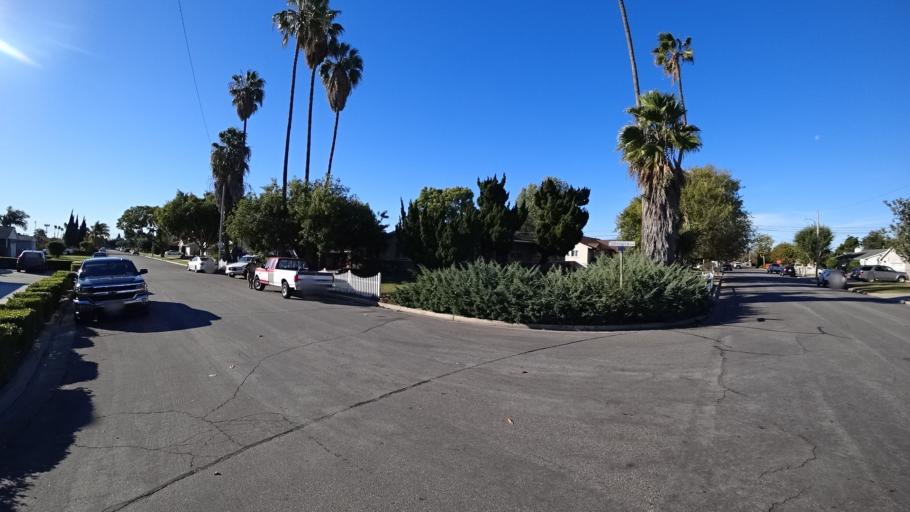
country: US
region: California
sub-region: Orange County
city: Garden Grove
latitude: 33.7698
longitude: -117.9664
